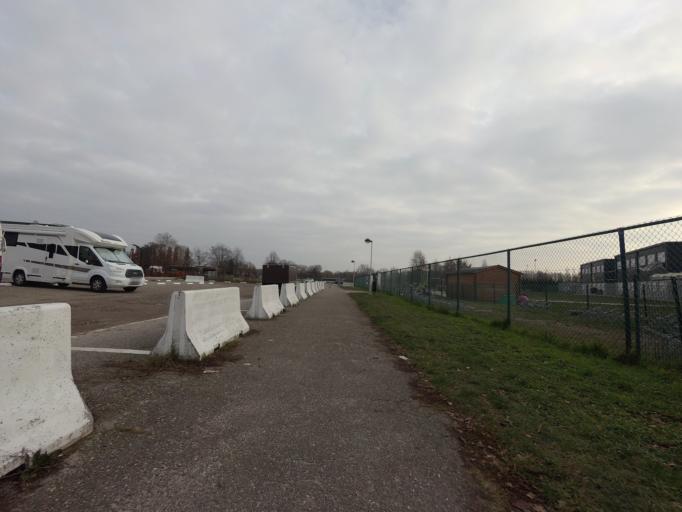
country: BE
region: Flanders
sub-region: Provincie Antwerpen
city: Borsbeek
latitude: 51.2194
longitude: 4.4840
